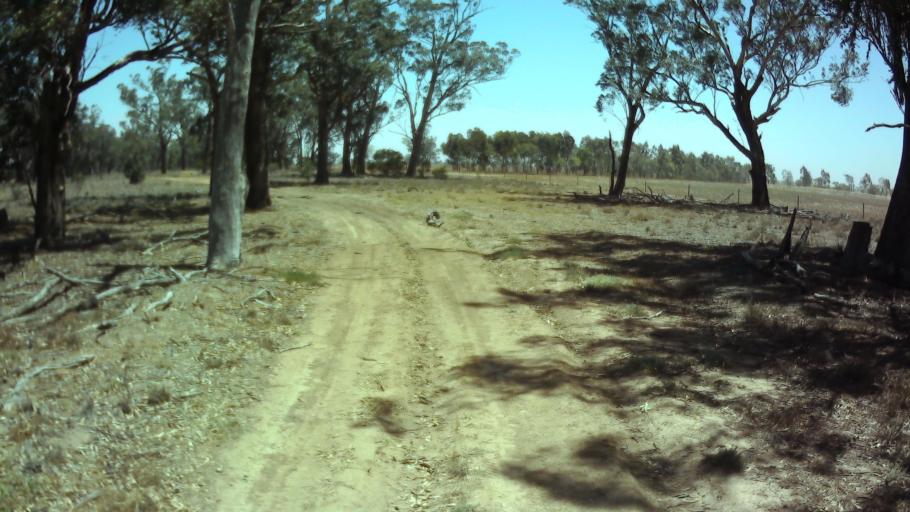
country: AU
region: New South Wales
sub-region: Weddin
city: Grenfell
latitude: -34.0574
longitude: 147.8180
